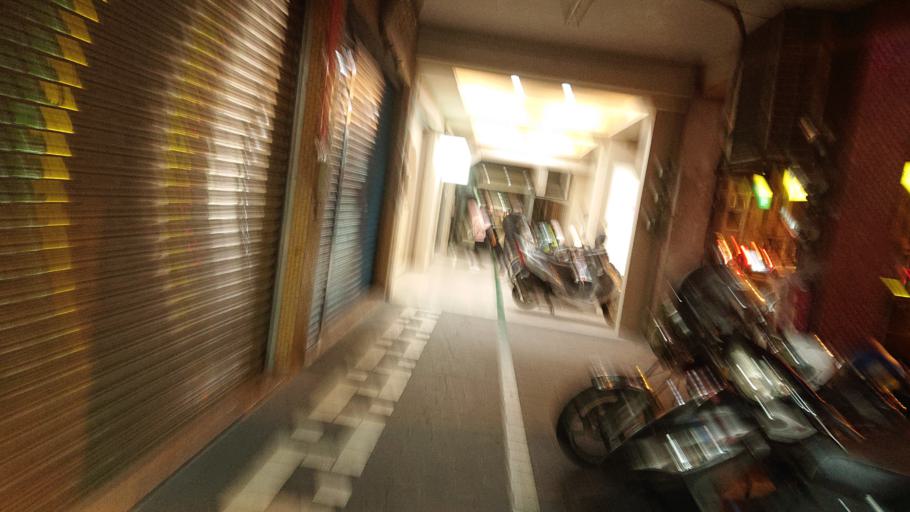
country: TW
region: Taiwan
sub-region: Tainan
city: Tainan
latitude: 22.9931
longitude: 120.2041
